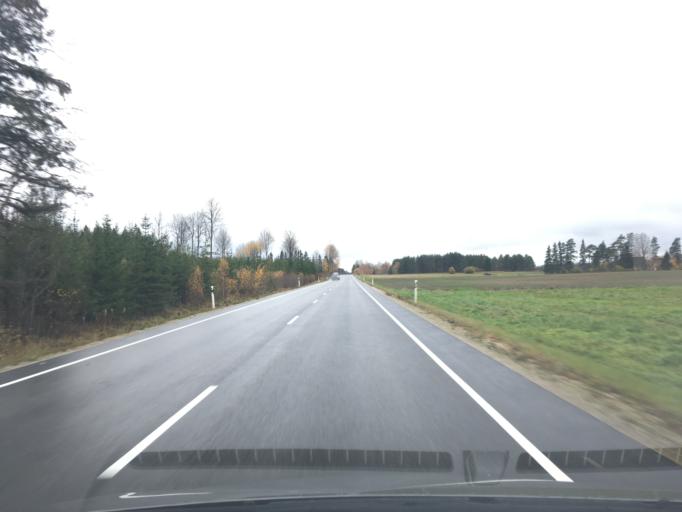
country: EE
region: Jogevamaa
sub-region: Tabivere vald
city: Tabivere
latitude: 58.4493
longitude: 26.5188
